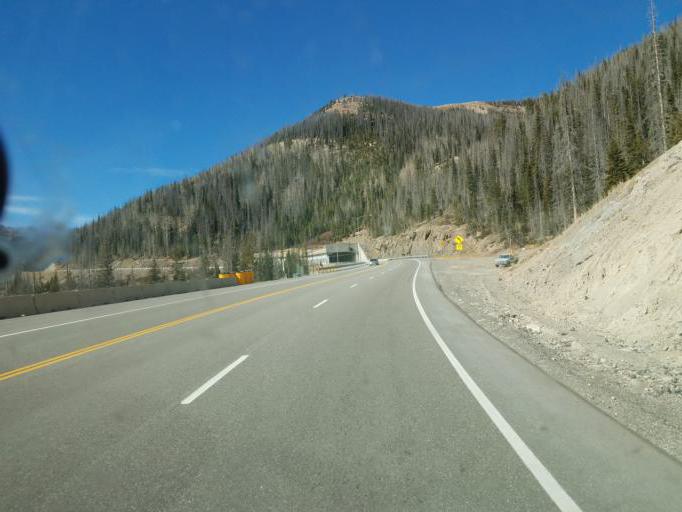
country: US
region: Colorado
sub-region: Archuleta County
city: Pagosa Springs
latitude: 37.4790
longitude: -106.7764
